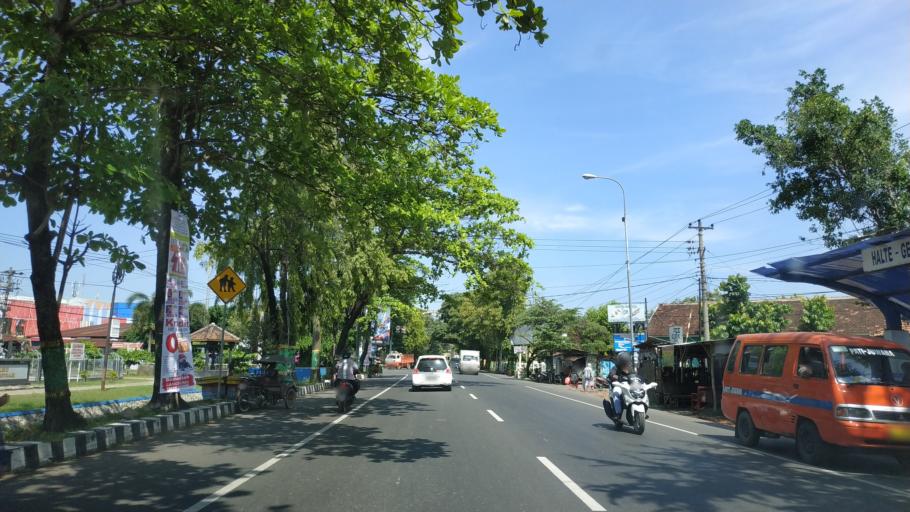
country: ID
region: Central Java
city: Baran
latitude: -6.7520
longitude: 111.0530
